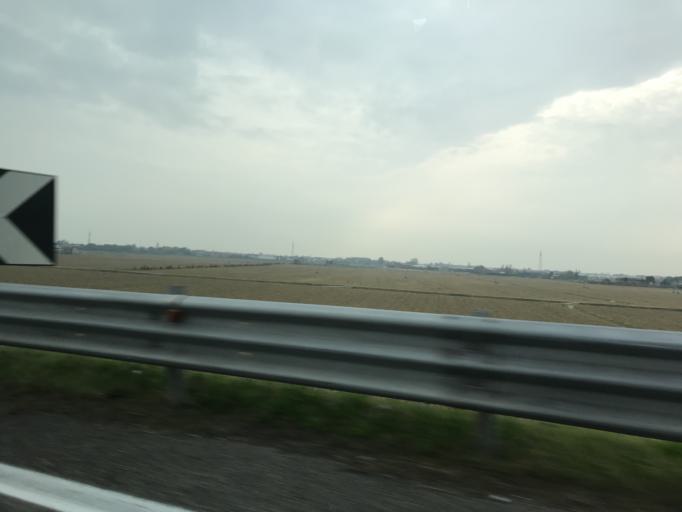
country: IT
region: Veneto
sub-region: Provincia di Venezia
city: Marcon-Gaggio-Colmello
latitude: 45.5788
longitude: 12.2906
